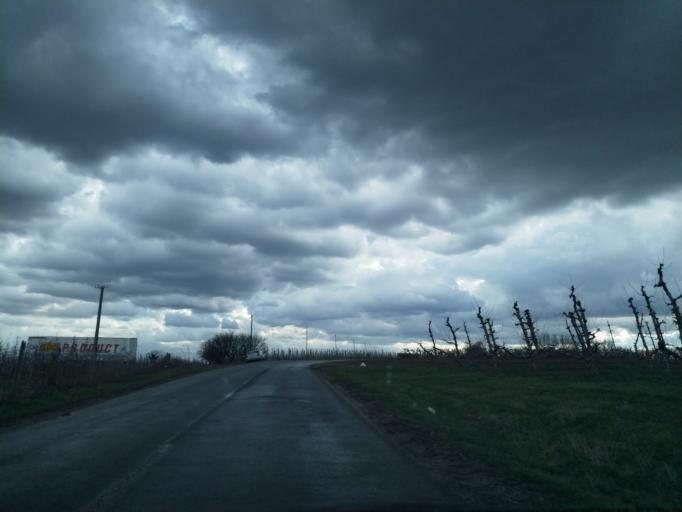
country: RS
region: Central Serbia
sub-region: Belgrade
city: Grocka
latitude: 44.6397
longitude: 20.7510
